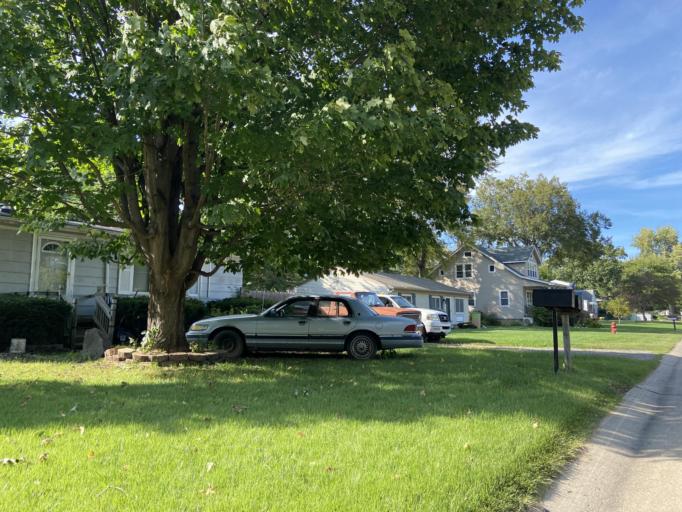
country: US
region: Michigan
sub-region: Oakland County
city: Farmington
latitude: 42.4481
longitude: -83.3196
